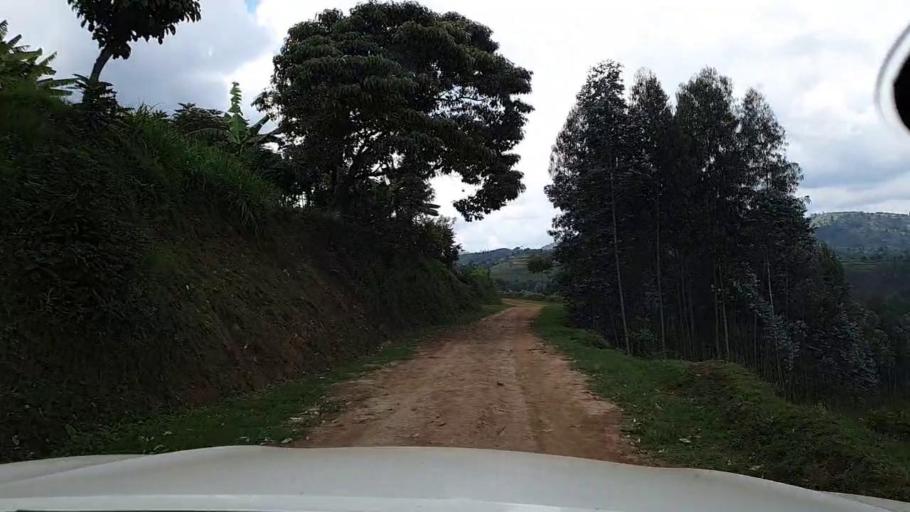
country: RW
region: Southern Province
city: Nzega
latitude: -2.6380
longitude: 29.4830
